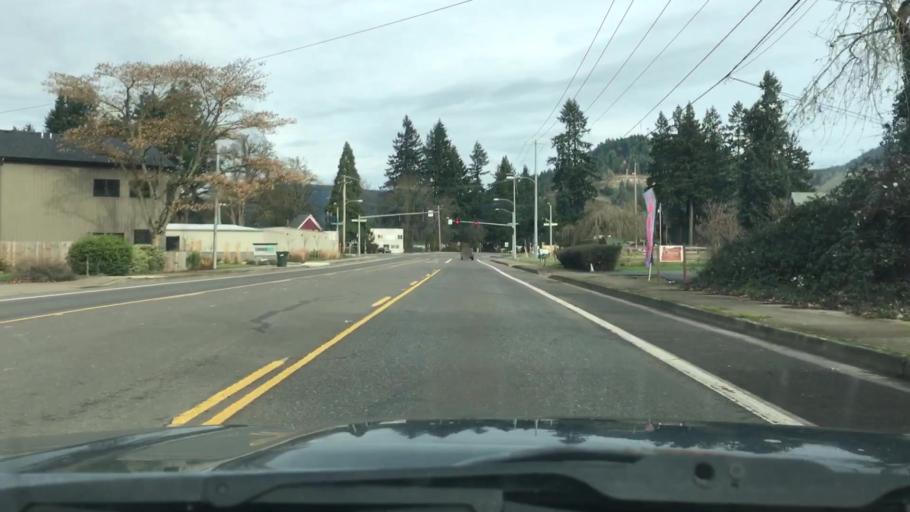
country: US
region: Oregon
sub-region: Lane County
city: Coburg
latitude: 44.1042
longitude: -123.0585
